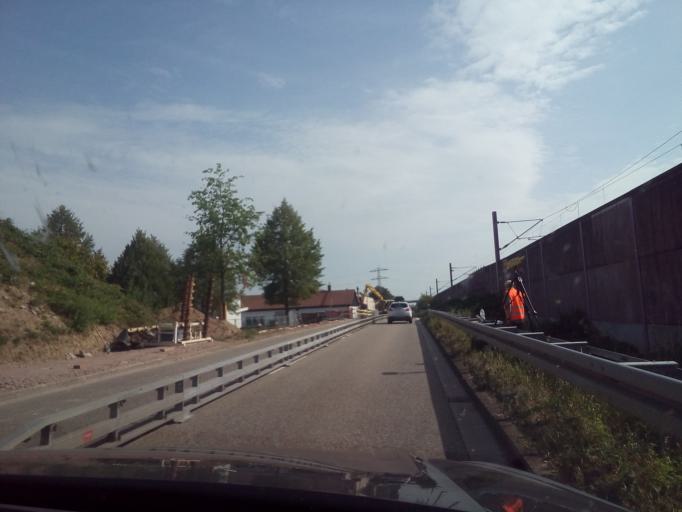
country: DE
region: Baden-Wuerttemberg
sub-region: Karlsruhe Region
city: Sinzheim
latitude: 48.7681
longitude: 8.1665
